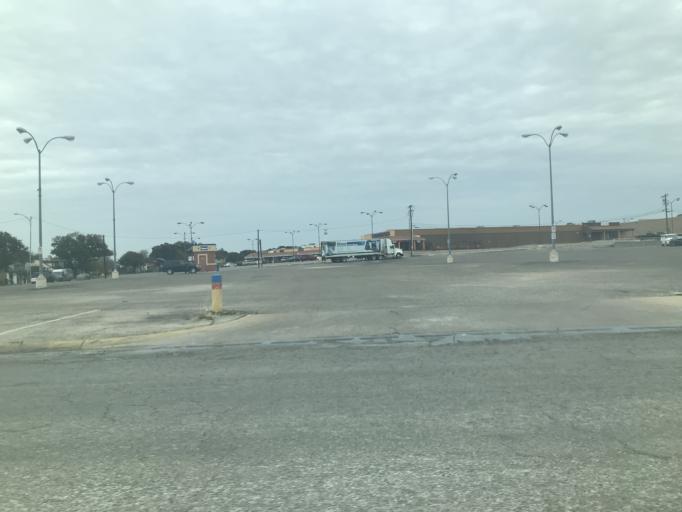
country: US
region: Texas
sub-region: Tom Green County
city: San Angelo
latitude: 31.4215
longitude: -100.4751
